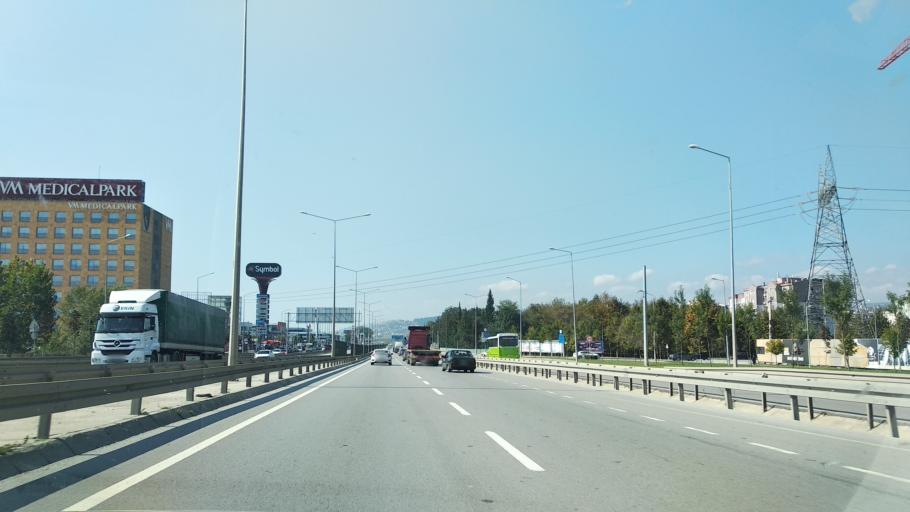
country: TR
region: Kocaeli
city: Kullar
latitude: 40.7593
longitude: 29.9829
